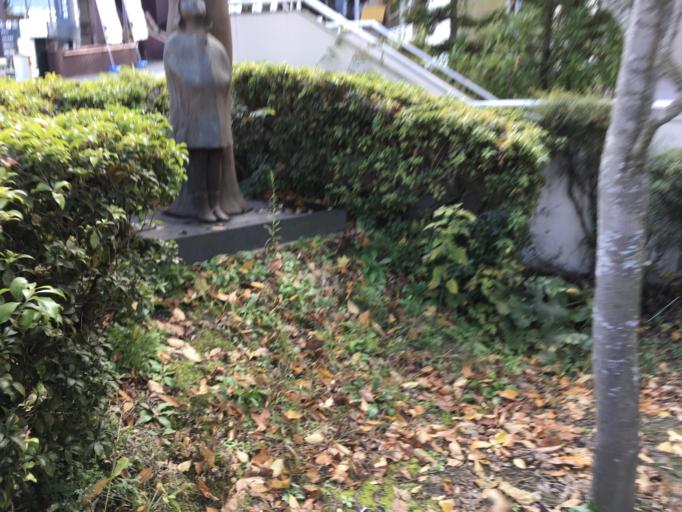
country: JP
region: Iwate
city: Tono
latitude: 39.3282
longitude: 141.5288
